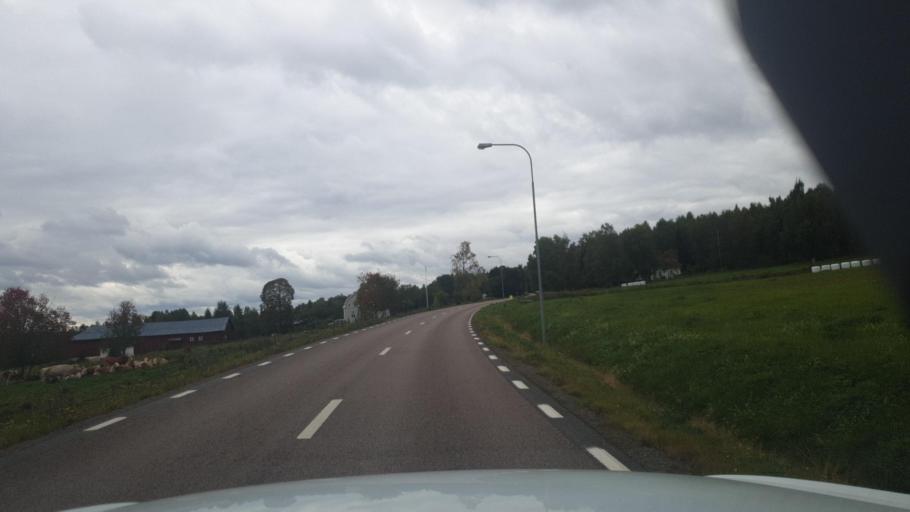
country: SE
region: Vaermland
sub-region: Sunne Kommun
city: Sunne
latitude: 59.8942
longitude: 12.9181
